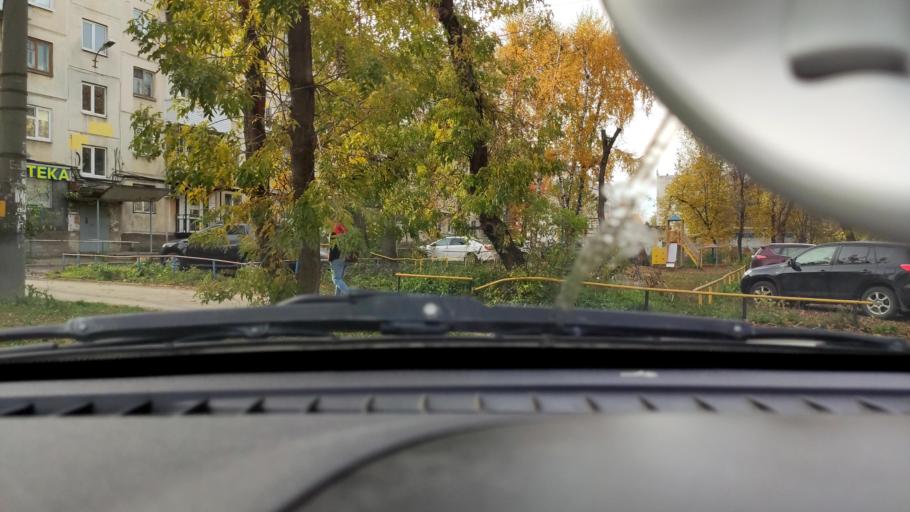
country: RU
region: Perm
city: Perm
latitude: 58.0062
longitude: 56.2131
